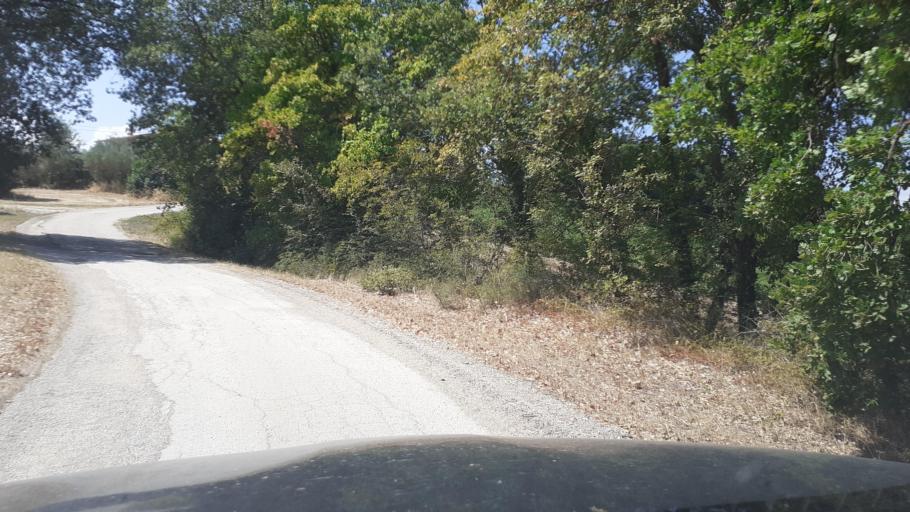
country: IT
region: Abruzzo
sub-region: Provincia di Chieti
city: Santa Maria Imbaro
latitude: 42.2101
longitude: 14.4740
